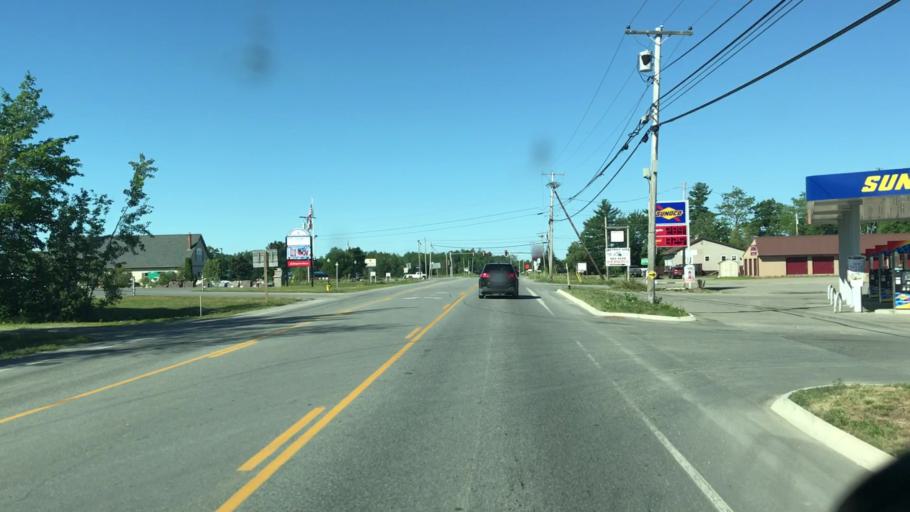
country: US
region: Maine
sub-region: Penobscot County
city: Lincoln
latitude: 45.3550
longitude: -68.5298
